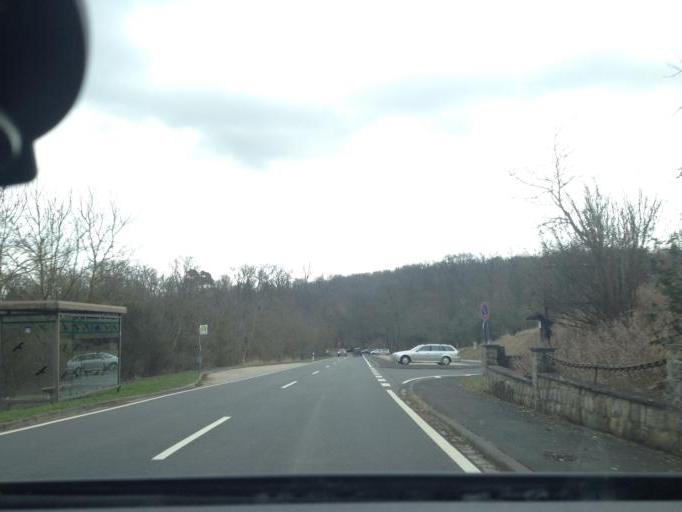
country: DE
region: Bavaria
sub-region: Regierungsbezirk Unterfranken
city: Wuerzburg
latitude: 49.7354
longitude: 9.8771
